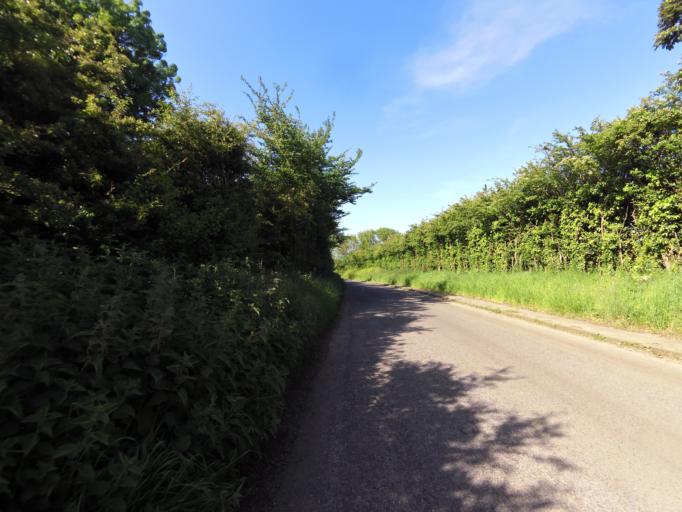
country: GB
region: England
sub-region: Suffolk
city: Felixstowe
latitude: 51.9970
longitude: 1.4123
